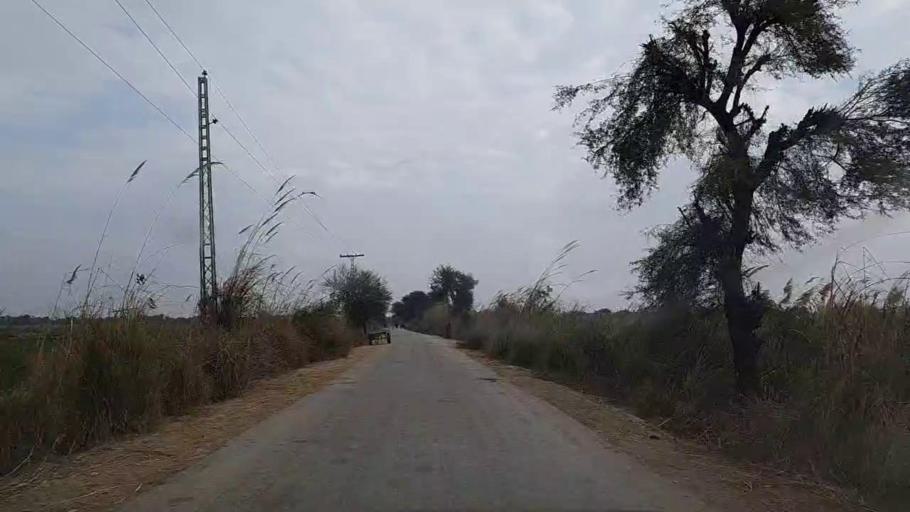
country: PK
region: Sindh
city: Sanghar
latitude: 26.2303
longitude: 68.9914
